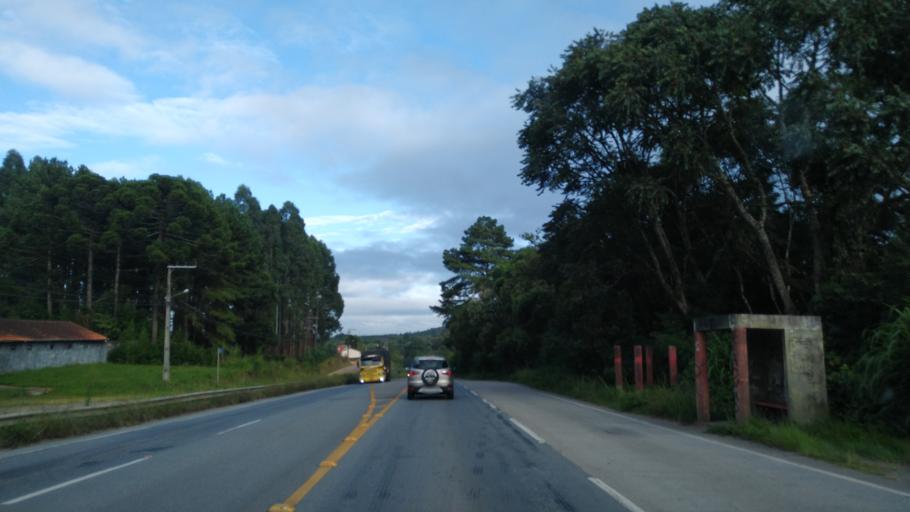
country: BR
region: Santa Catarina
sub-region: Rio Negrinho
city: Rio Negrinho
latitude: -26.2460
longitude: -49.4518
